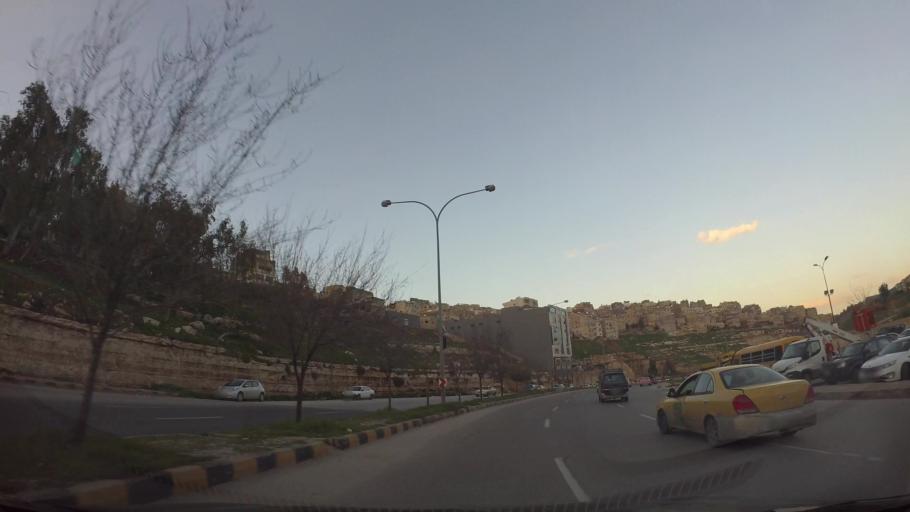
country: JO
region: Amman
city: Al Bunayyat ash Shamaliyah
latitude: 31.9265
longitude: 35.9111
